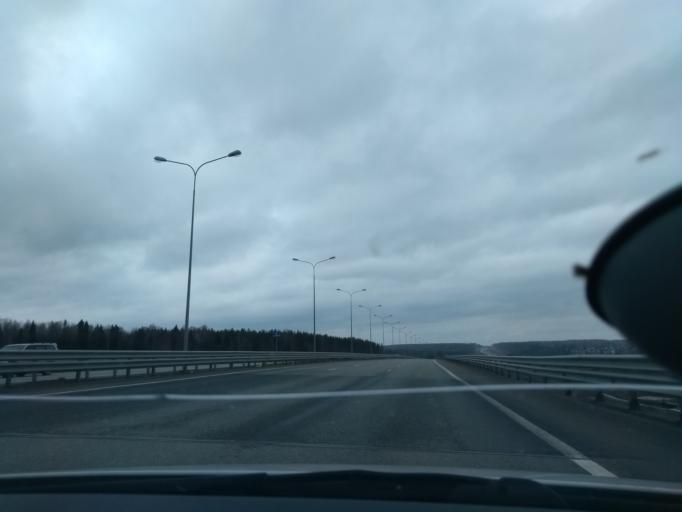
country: RU
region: Perm
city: Bershet'
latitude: 57.7072
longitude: 56.3683
